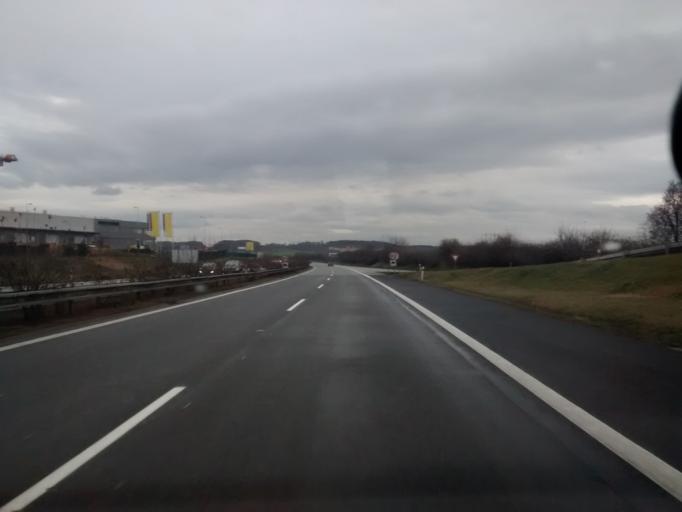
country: CZ
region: Central Bohemia
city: Odolena Voda
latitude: 50.2463
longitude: 14.3754
